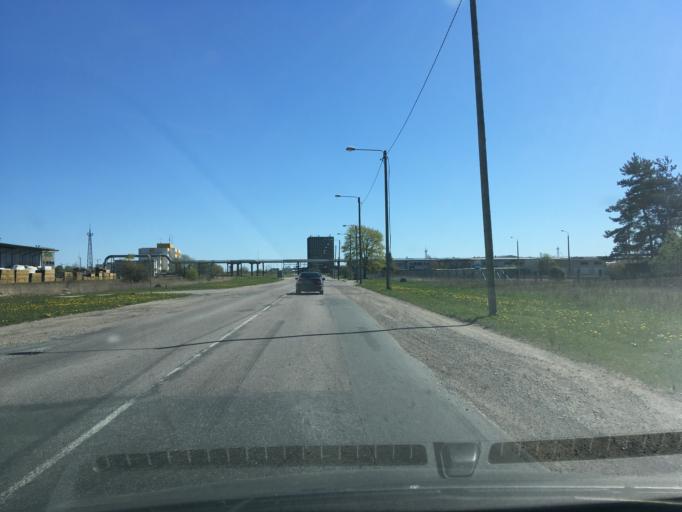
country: EE
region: Harju
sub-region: Joelaehtme vald
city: Loo
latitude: 59.4582
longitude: 24.9355
